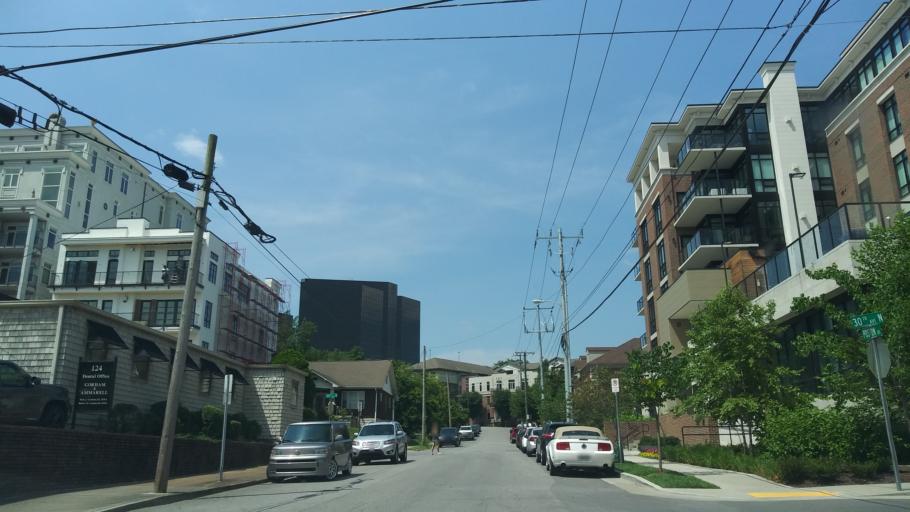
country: US
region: Tennessee
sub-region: Davidson County
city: Nashville
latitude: 36.1454
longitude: -86.8149
